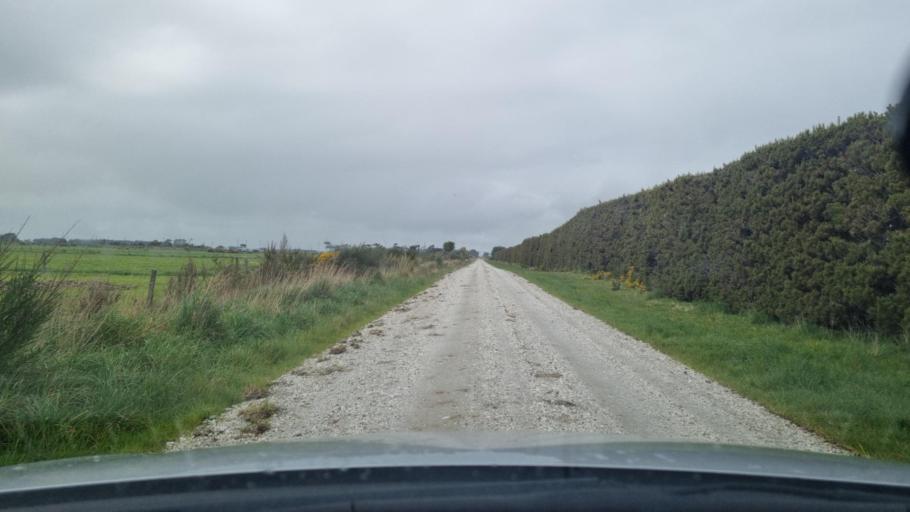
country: NZ
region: Southland
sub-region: Invercargill City
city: Invercargill
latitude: -46.4990
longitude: 168.4129
